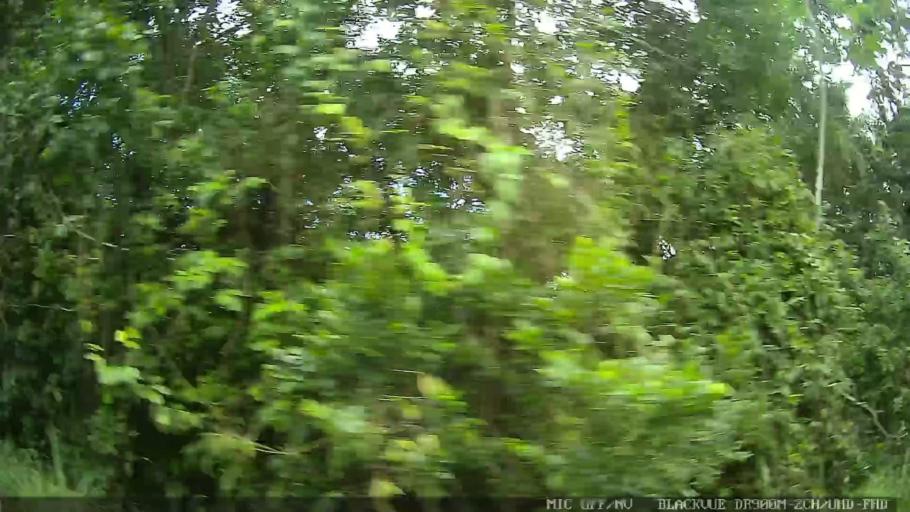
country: BR
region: Sao Paulo
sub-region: Iguape
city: Iguape
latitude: -24.6663
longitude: -47.4355
